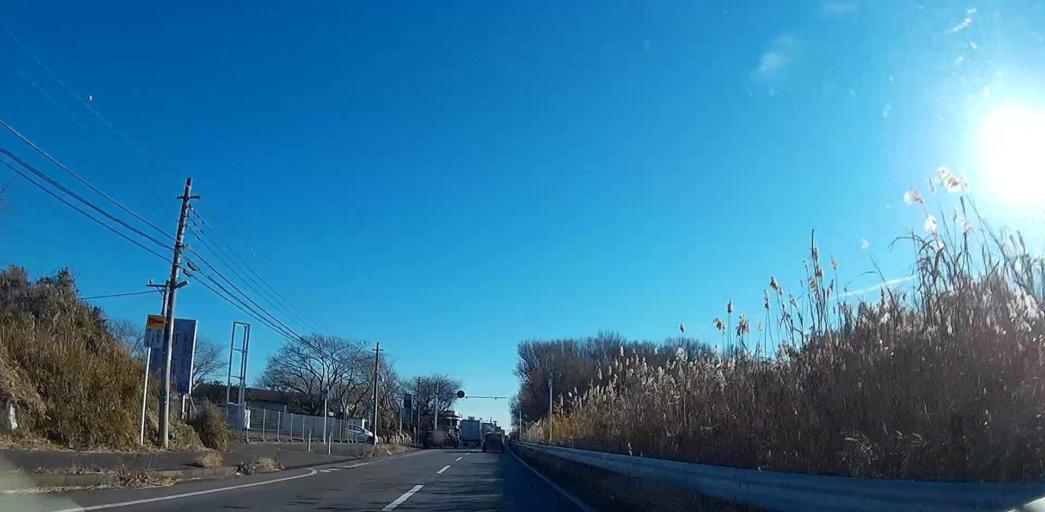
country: JP
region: Chiba
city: Shiroi
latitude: 35.7845
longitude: 140.0120
